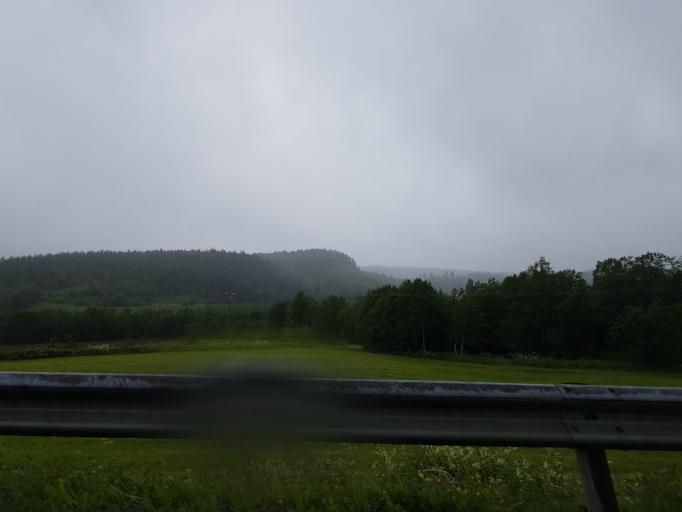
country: NO
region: Sor-Trondelag
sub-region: Selbu
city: Mebonden
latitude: 63.3881
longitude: 11.0726
